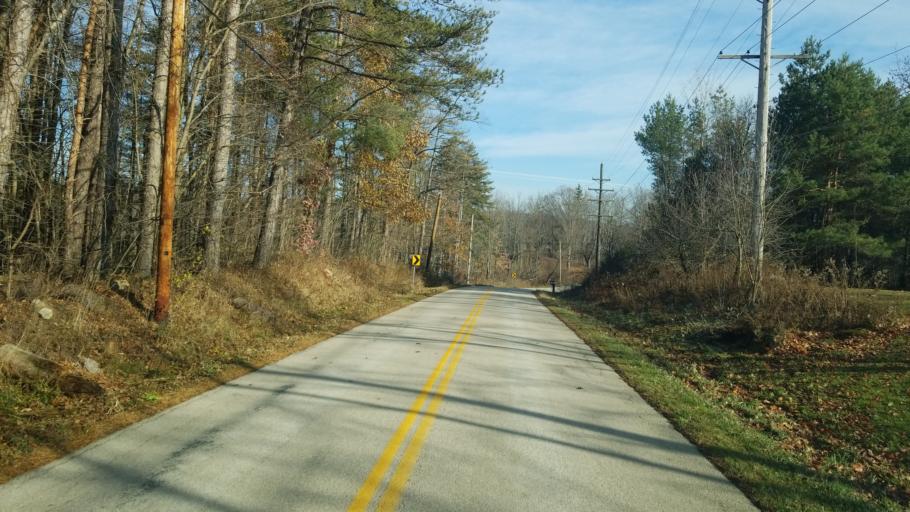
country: US
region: Ohio
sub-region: Ashtabula County
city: North Kingsville
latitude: 41.8425
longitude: -80.6775
